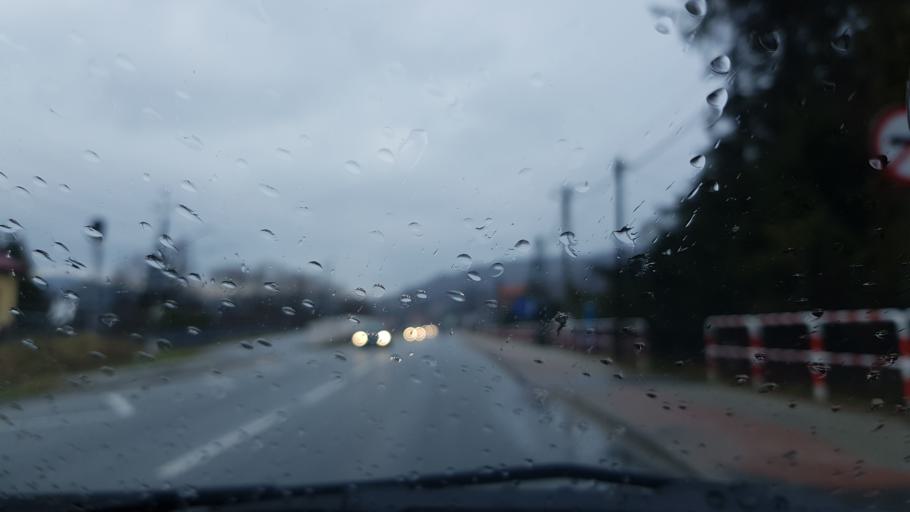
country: PL
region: Lesser Poland Voivodeship
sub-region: Powiat suski
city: Sucha Beskidzka
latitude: 49.7360
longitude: 19.5583
